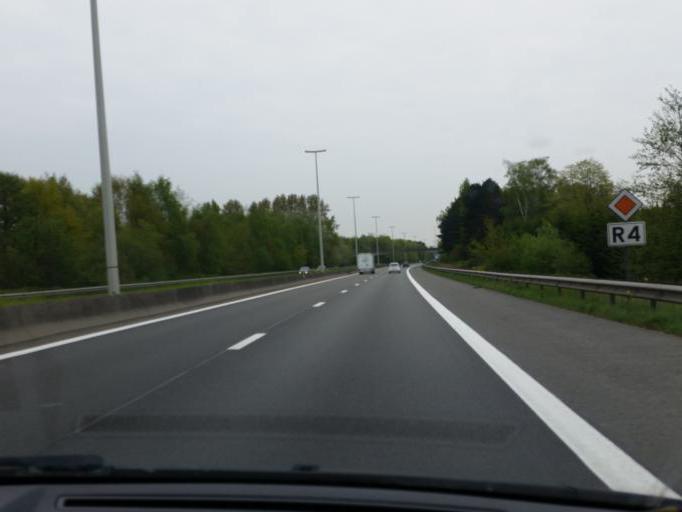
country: BE
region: Flanders
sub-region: Provincie Oost-Vlaanderen
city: Melle
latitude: 51.0161
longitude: 3.7996
